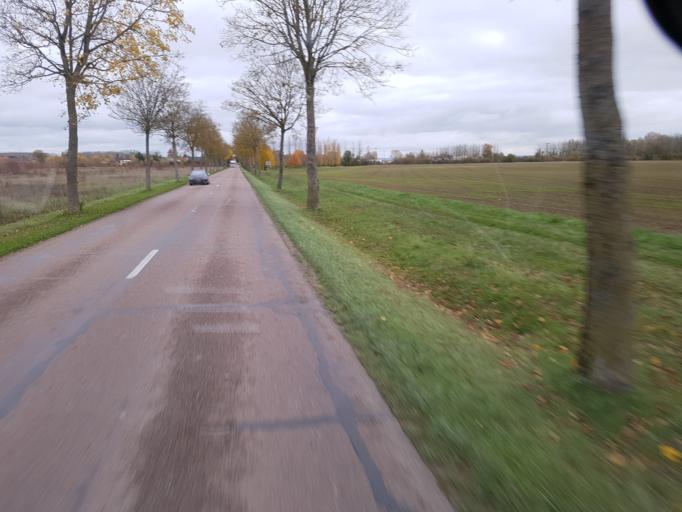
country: FR
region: Champagne-Ardenne
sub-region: Departement de l'Aube
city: Mery-sur-Seine
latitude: 48.5164
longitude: 3.8774
